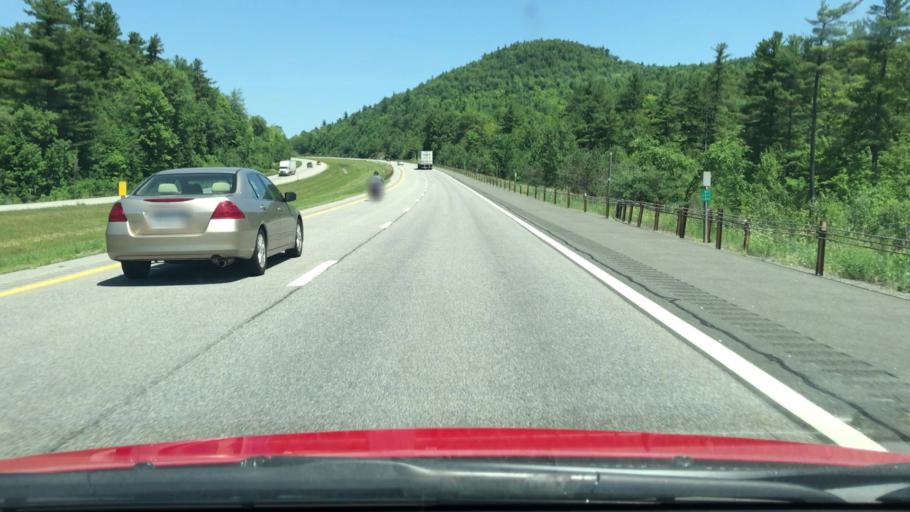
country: US
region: New York
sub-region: Essex County
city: Keeseville
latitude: 44.3880
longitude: -73.5051
